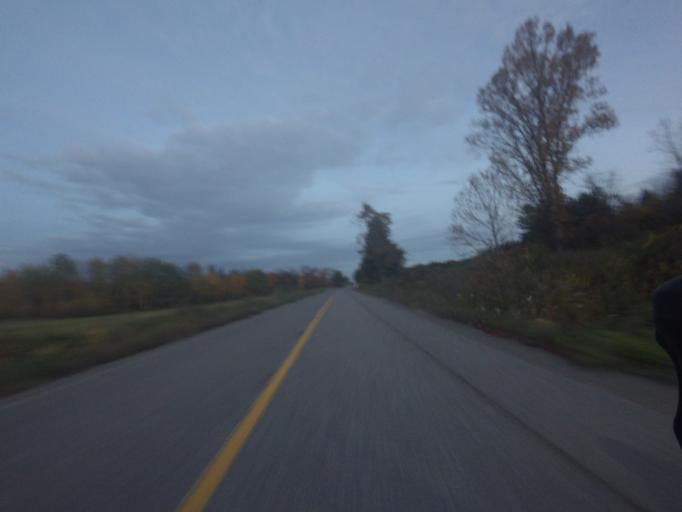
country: CA
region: Ontario
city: Renfrew
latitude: 45.3406
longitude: -76.9177
